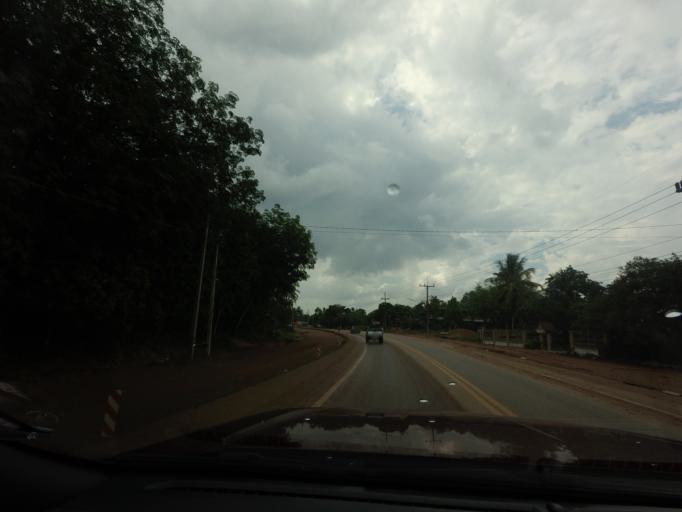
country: TH
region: Yala
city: Ban Nang Sata
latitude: 6.3246
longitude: 101.3037
